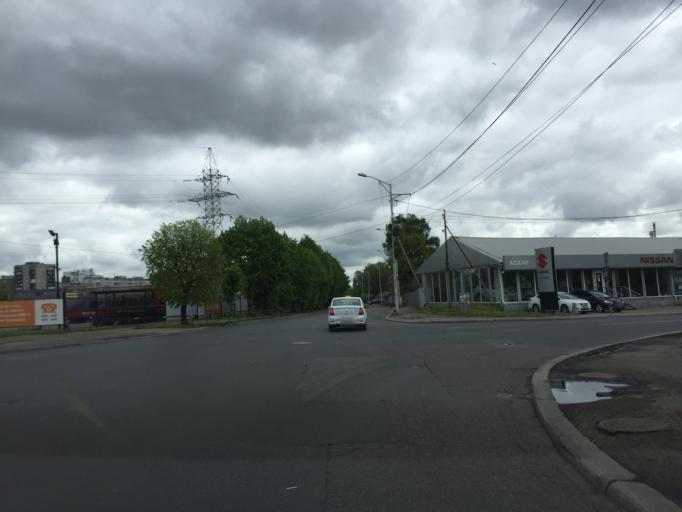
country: RU
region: Kaliningrad
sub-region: Gorod Kaliningrad
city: Kaliningrad
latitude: 54.7050
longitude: 20.4901
